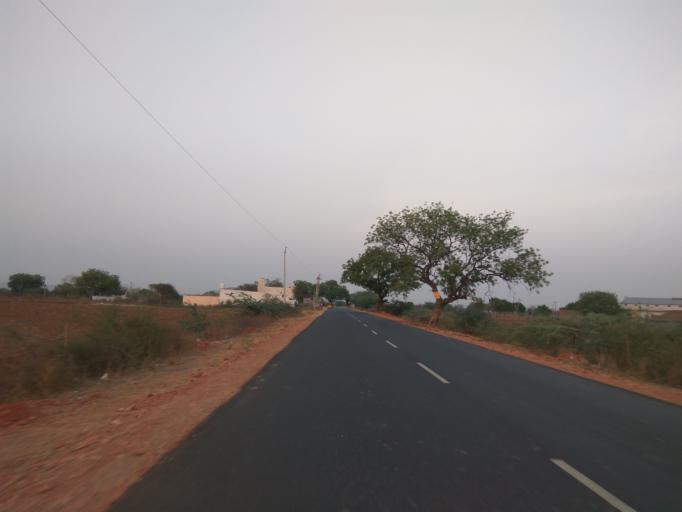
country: IN
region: Andhra Pradesh
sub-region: Prakasam
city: Markapur
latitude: 15.7525
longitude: 79.2236
